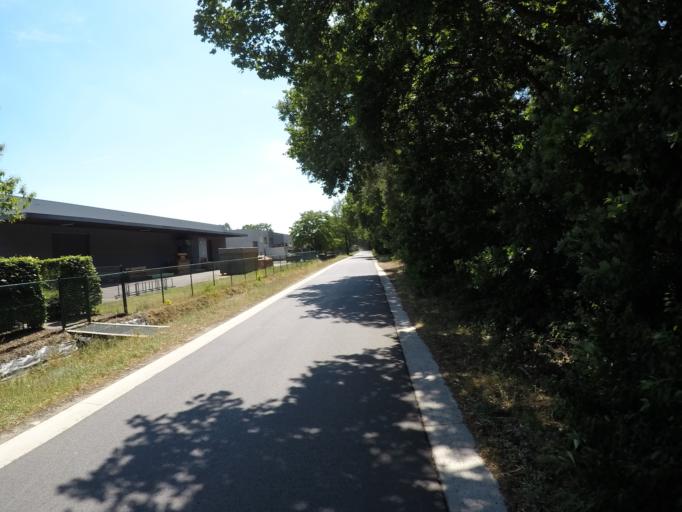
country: BE
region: Flanders
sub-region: Provincie Antwerpen
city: Wuustwezel
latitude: 51.3909
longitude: 4.5615
